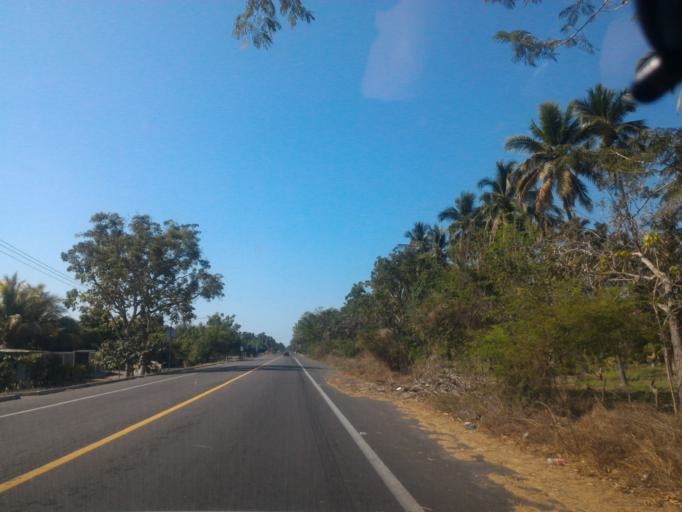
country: MX
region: Colima
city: Tecoman
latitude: 18.8974
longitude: -103.9157
